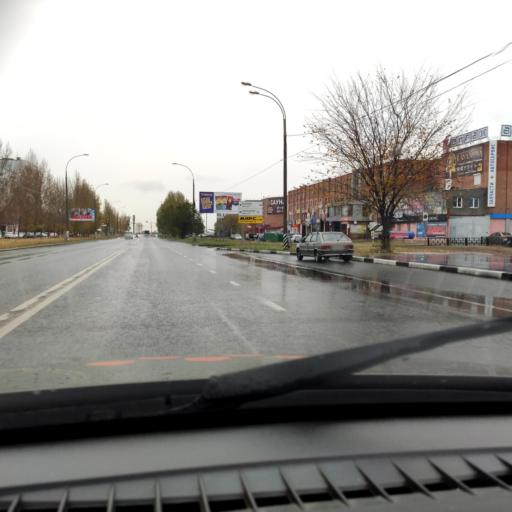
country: RU
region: Samara
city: Tol'yatti
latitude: 53.5446
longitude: 49.3463
